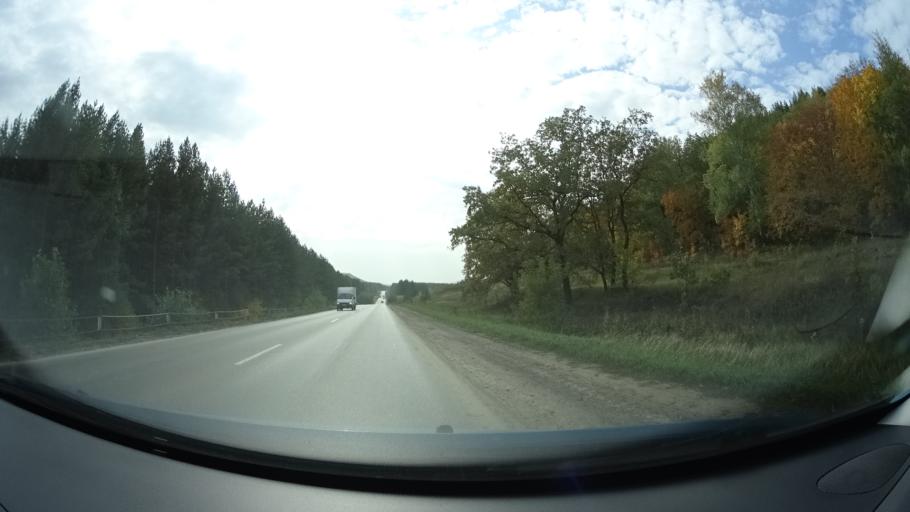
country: RU
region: Bashkortostan
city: Oktyabr'skiy
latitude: 54.5350
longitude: 53.5585
